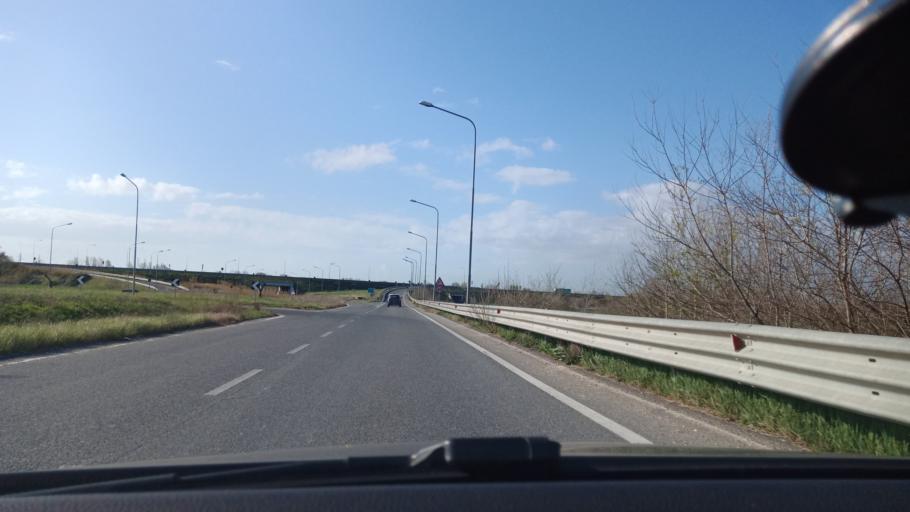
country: IT
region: Latium
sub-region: Citta metropolitana di Roma Capitale
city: Fiano Romano
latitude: 42.1559
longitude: 12.6423
